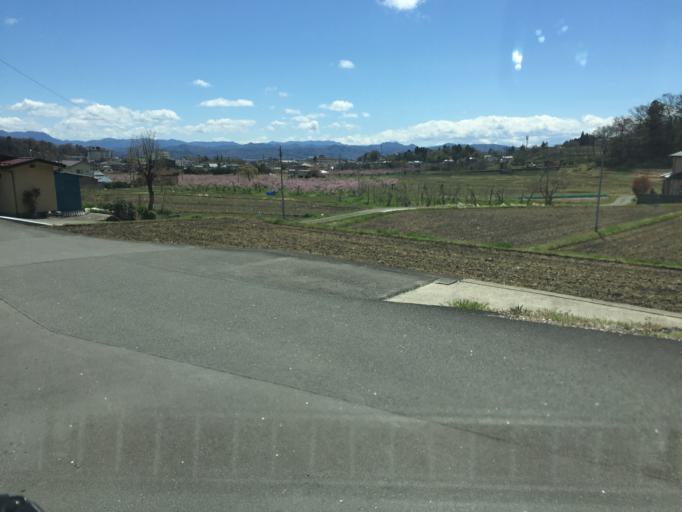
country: JP
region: Fukushima
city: Fukushima-shi
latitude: 37.8399
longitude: 140.4382
